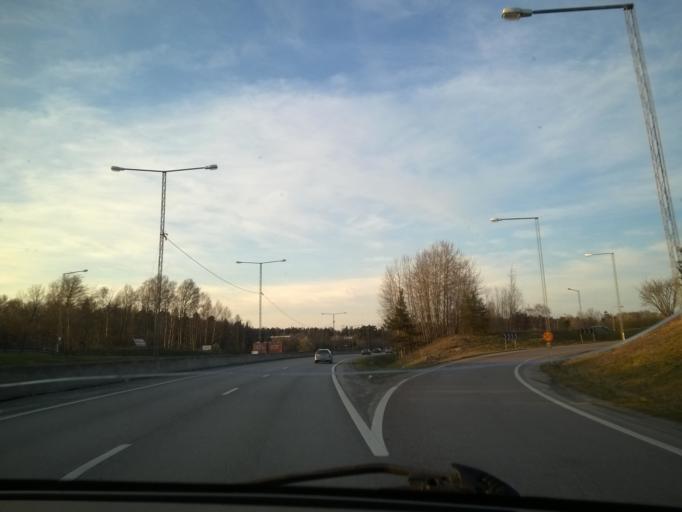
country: SE
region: Stockholm
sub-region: Stockholms Kommun
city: Kista
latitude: 59.3756
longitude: 17.9275
